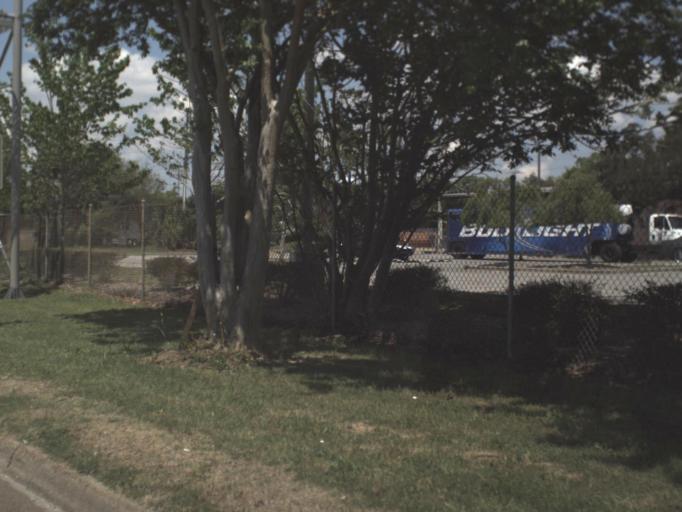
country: US
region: Florida
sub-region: Escambia County
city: Pensacola
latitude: 30.4171
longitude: -87.2066
